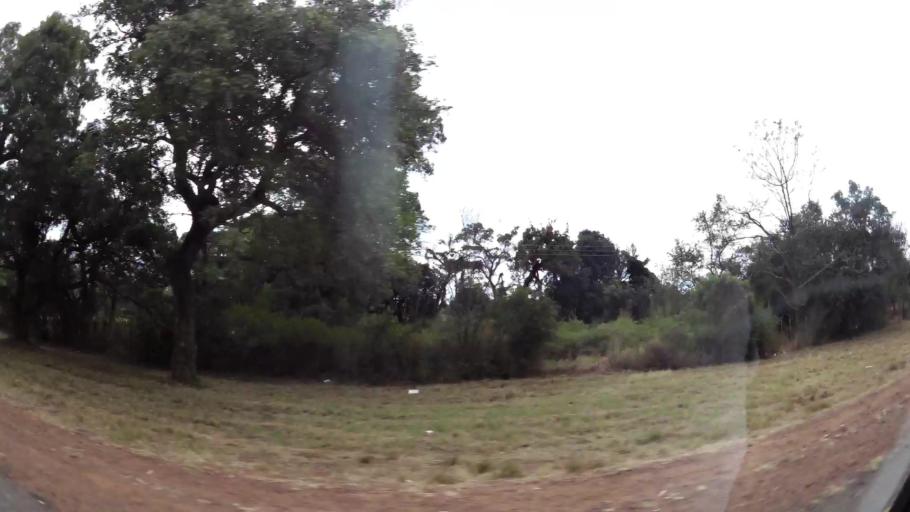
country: ZA
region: Limpopo
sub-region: Waterberg District Municipality
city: Modimolle
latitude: -24.6737
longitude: 28.4474
